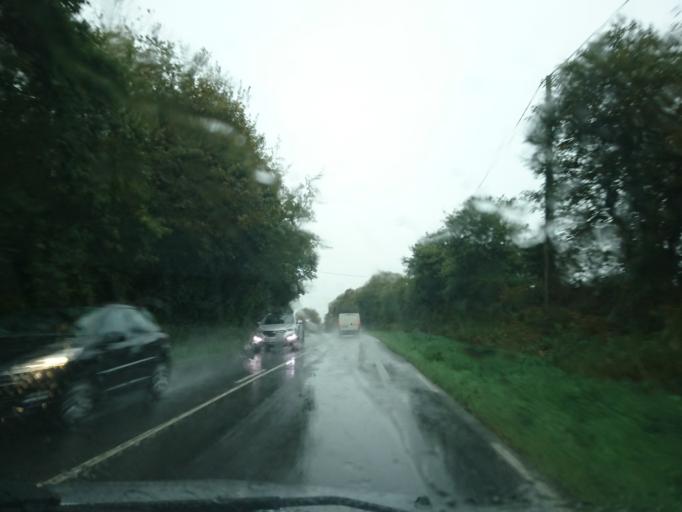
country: FR
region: Brittany
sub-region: Departement du Finistere
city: Plabennec
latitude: 48.4858
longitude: -4.4347
